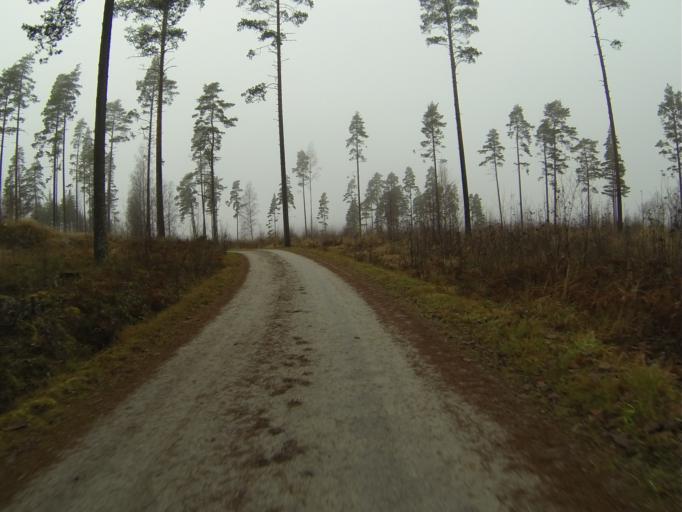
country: FI
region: Varsinais-Suomi
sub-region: Salo
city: Halikko
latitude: 60.4082
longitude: 22.9538
